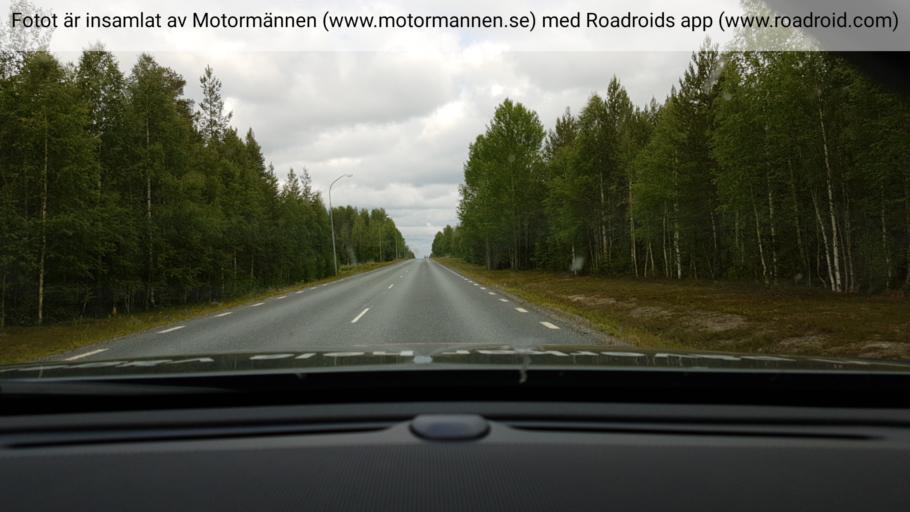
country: SE
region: Vaesterbotten
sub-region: Mala Kommun
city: Mala
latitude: 64.9924
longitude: 18.4906
